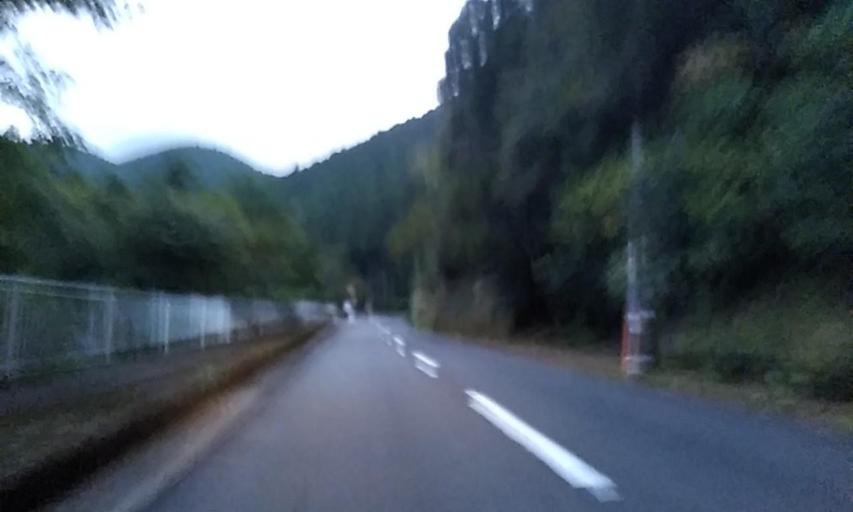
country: JP
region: Wakayama
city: Shingu
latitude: 33.7413
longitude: 135.9334
